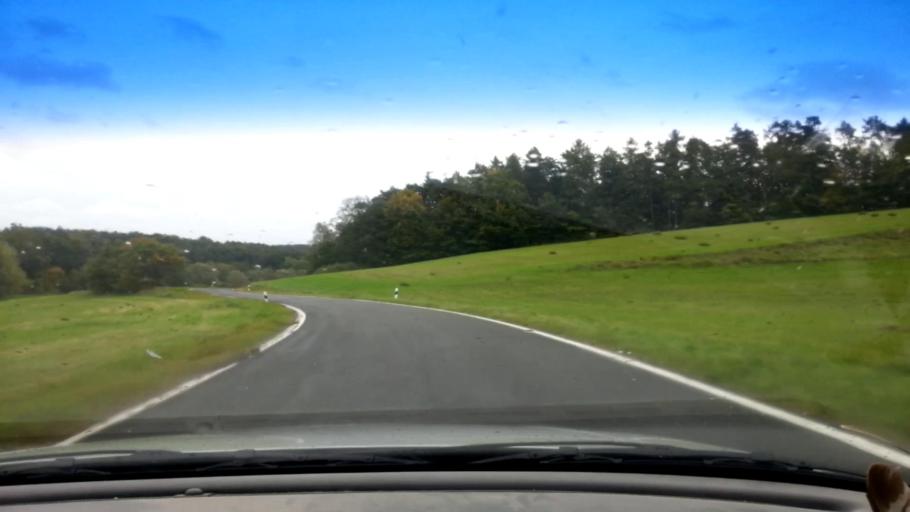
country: DE
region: Bavaria
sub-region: Regierungsbezirk Unterfranken
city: Kirchlauter
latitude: 50.0305
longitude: 10.7292
